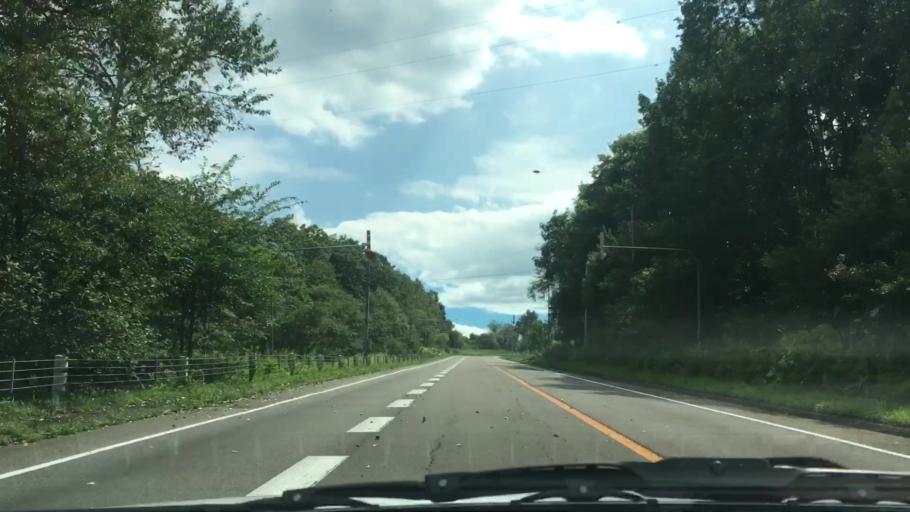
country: JP
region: Hokkaido
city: Otofuke
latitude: 43.2802
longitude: 143.4065
